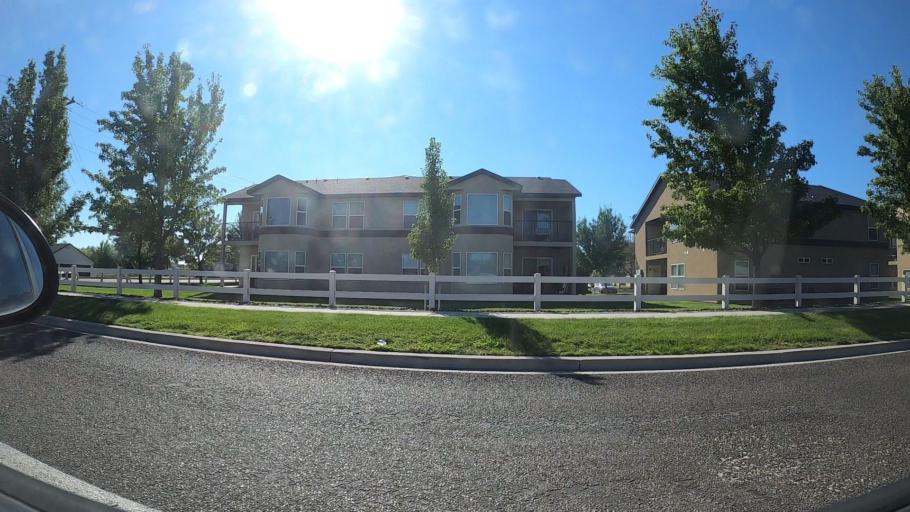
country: US
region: Idaho
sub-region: Canyon County
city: Nampa
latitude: 43.5999
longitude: -116.6132
